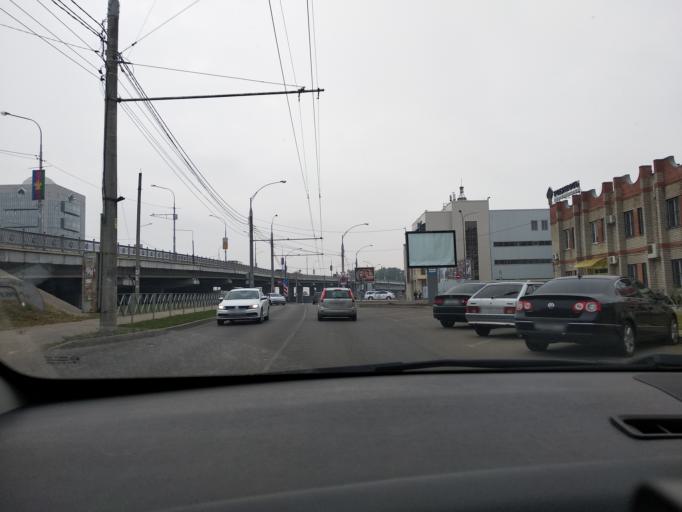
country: RU
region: Krasnodarskiy
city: Krasnodar
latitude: 45.0387
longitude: 38.9548
